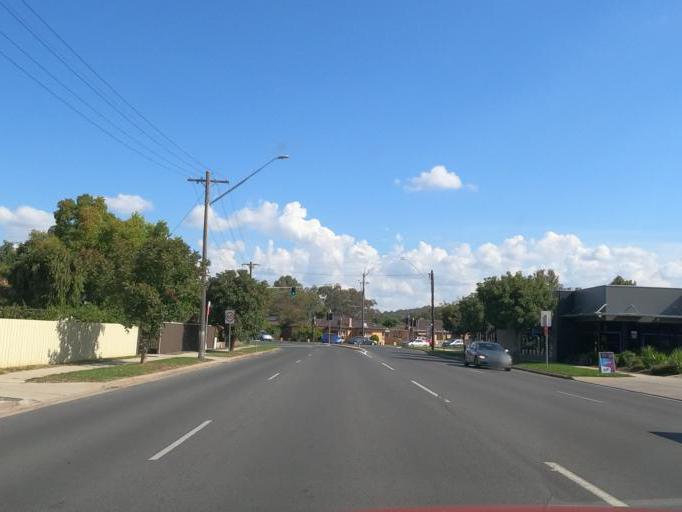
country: AU
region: New South Wales
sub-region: Albury Municipality
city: North Albury
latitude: -36.0565
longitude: 146.9279
